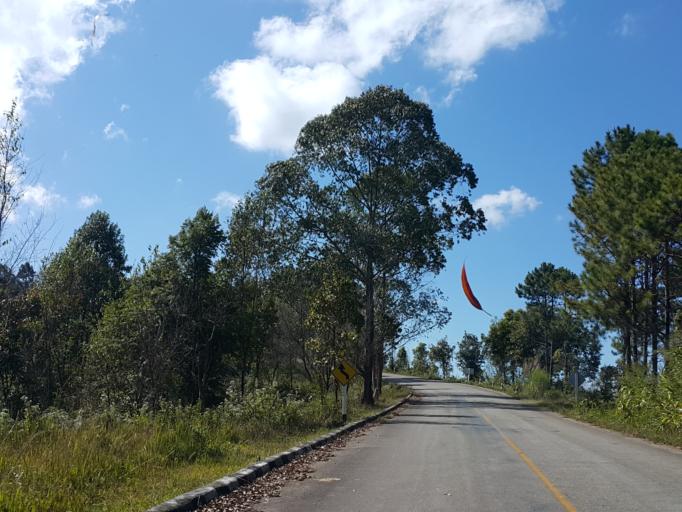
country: TH
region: Chiang Mai
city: Wiang Haeng
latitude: 19.5192
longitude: 98.7602
